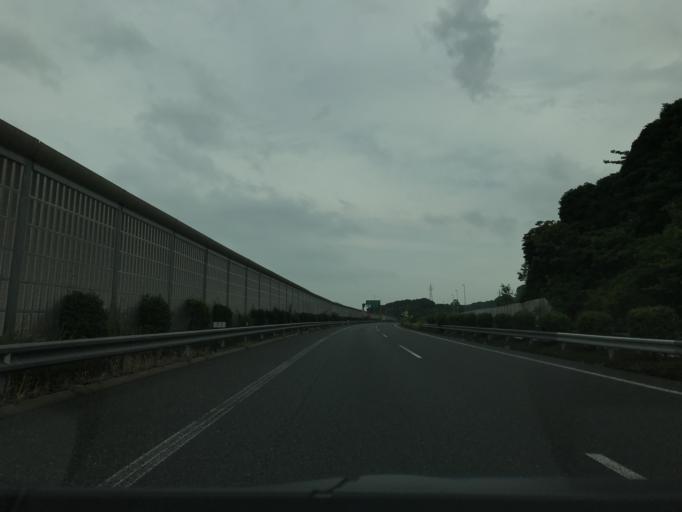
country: JP
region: Fukuoka
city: Kanda
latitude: 33.7978
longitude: 130.9622
